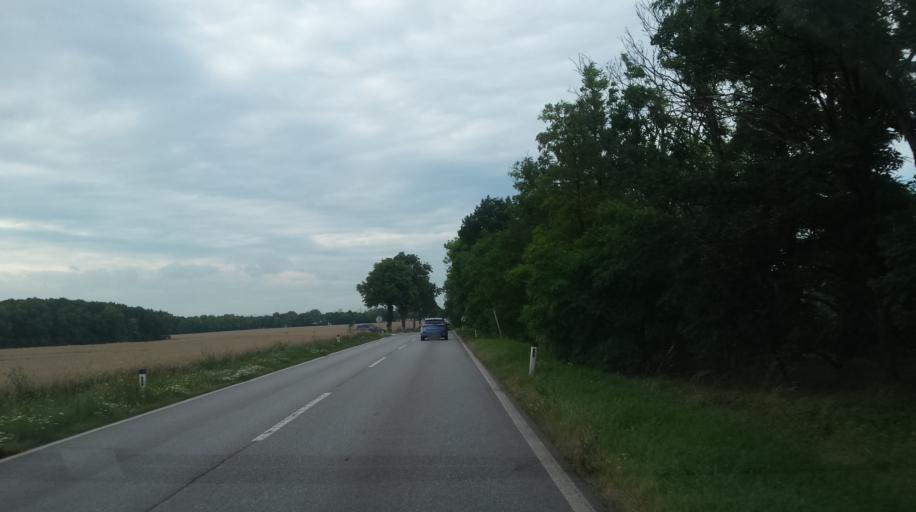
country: AT
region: Lower Austria
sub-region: Politischer Bezirk Wien-Umgebung
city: Moosbrunn
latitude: 48.0516
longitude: 16.4612
